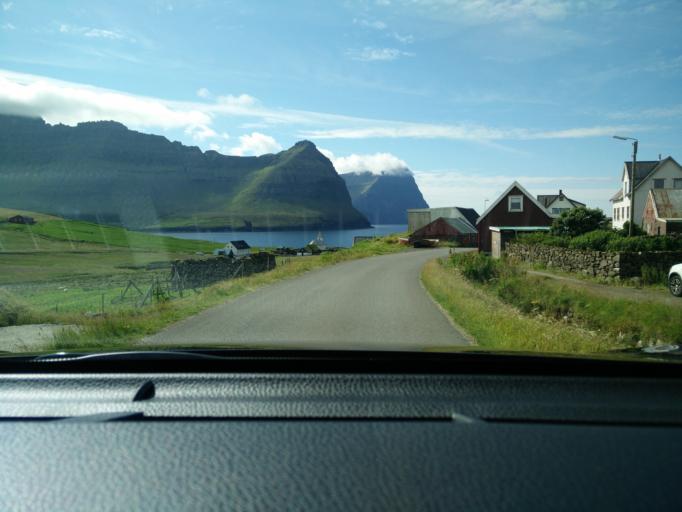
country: FO
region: Nordoyar
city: Klaksvik
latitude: 62.3603
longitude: -6.5356
